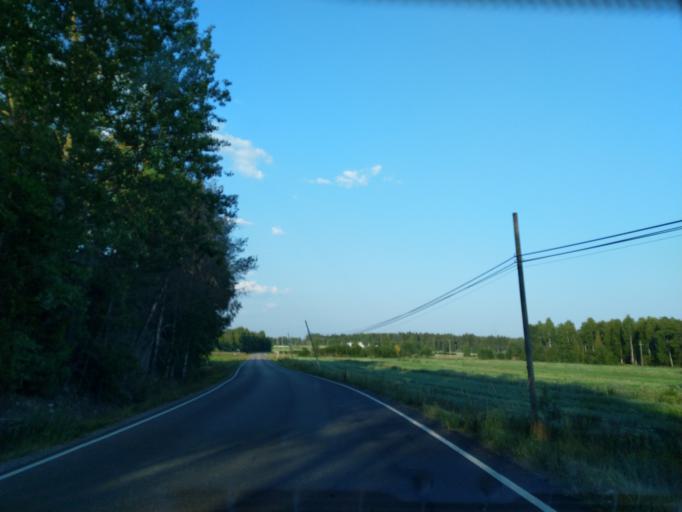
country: FI
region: Satakunta
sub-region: Pohjois-Satakunta
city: Honkajoki
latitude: 61.8200
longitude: 22.2444
